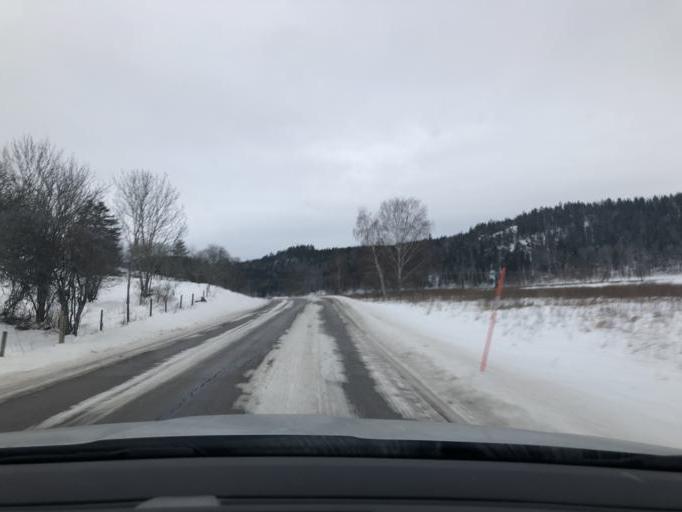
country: SE
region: OEstergoetland
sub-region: Kinda Kommun
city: Rimforsa
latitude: 58.0837
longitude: 15.8292
